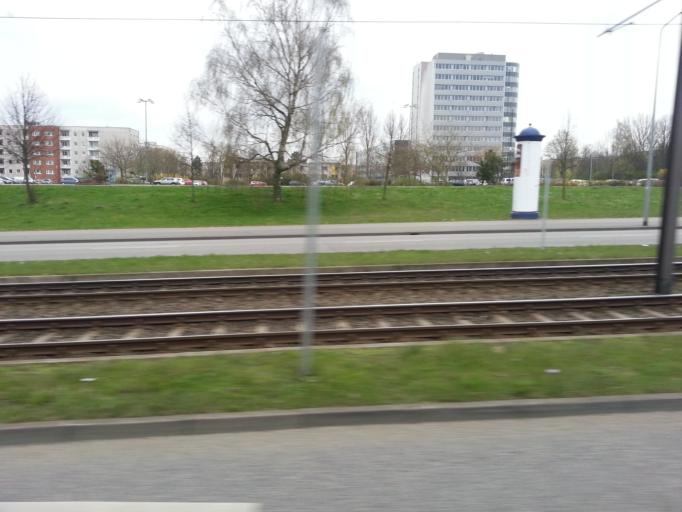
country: DE
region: Mecklenburg-Vorpommern
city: Rostock
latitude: 54.0761
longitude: 12.1228
